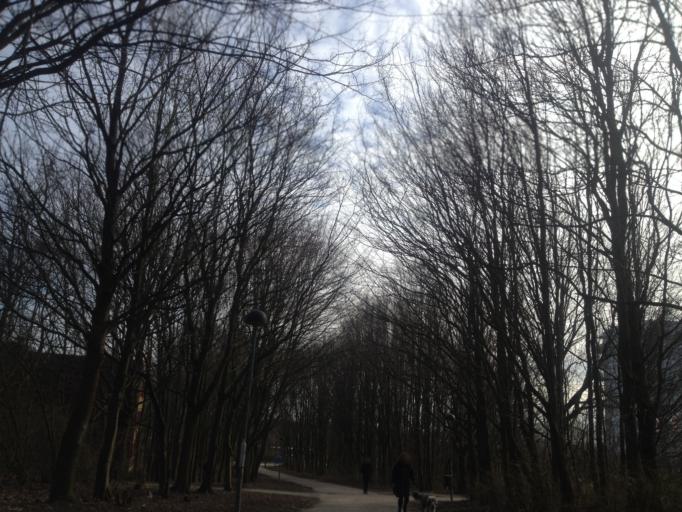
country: SE
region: Skane
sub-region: Lunds Kommun
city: Lund
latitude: 55.6957
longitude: 13.2440
